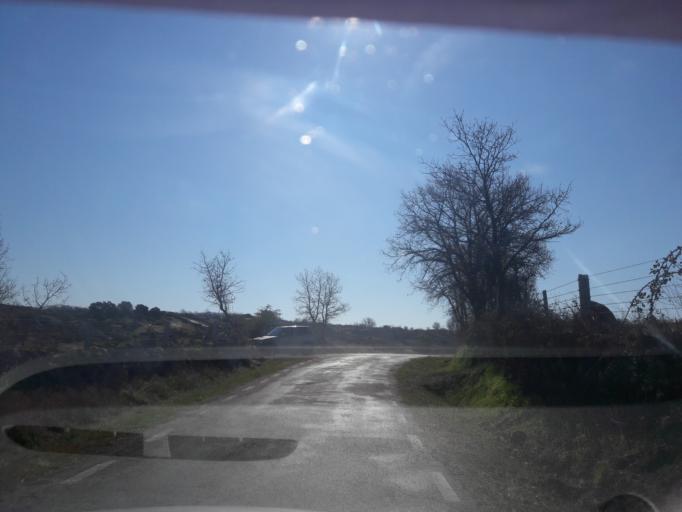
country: ES
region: Castille and Leon
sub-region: Provincia de Salamanca
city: Valsalabroso
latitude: 41.1581
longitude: -6.4910
